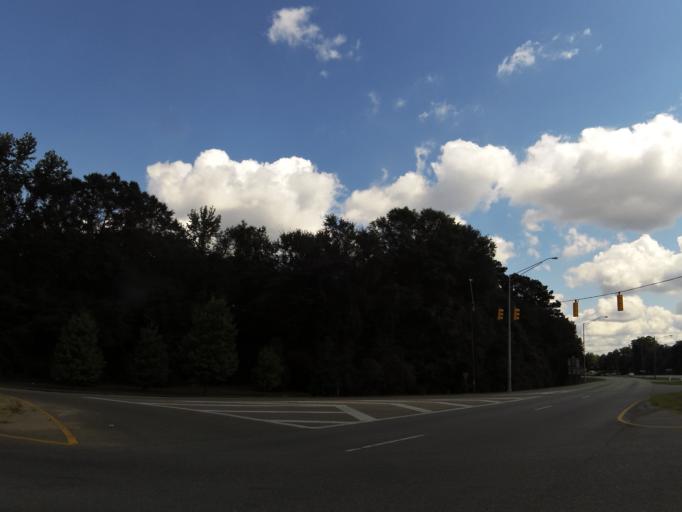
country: US
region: Alabama
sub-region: Dallas County
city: Selmont-West Selmont
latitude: 32.3698
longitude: -87.0048
